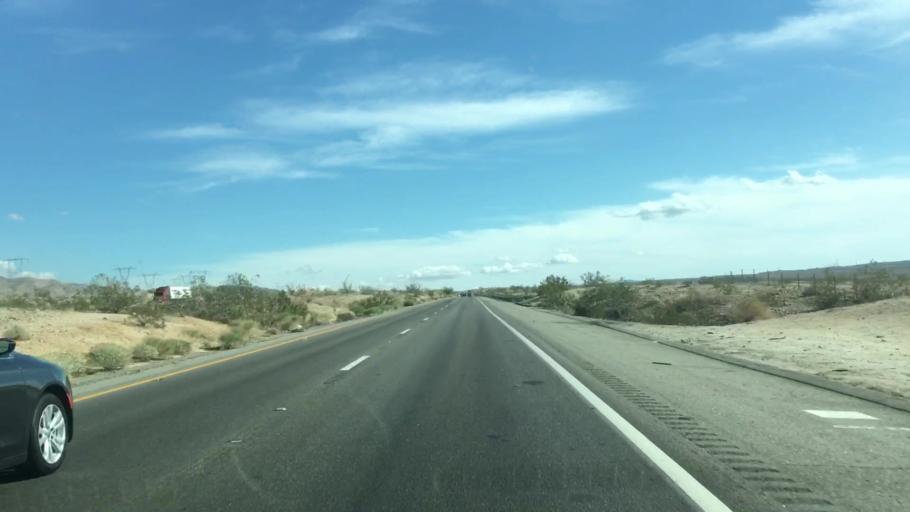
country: US
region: California
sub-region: Riverside County
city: Thermal
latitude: 33.6882
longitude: -116.0358
